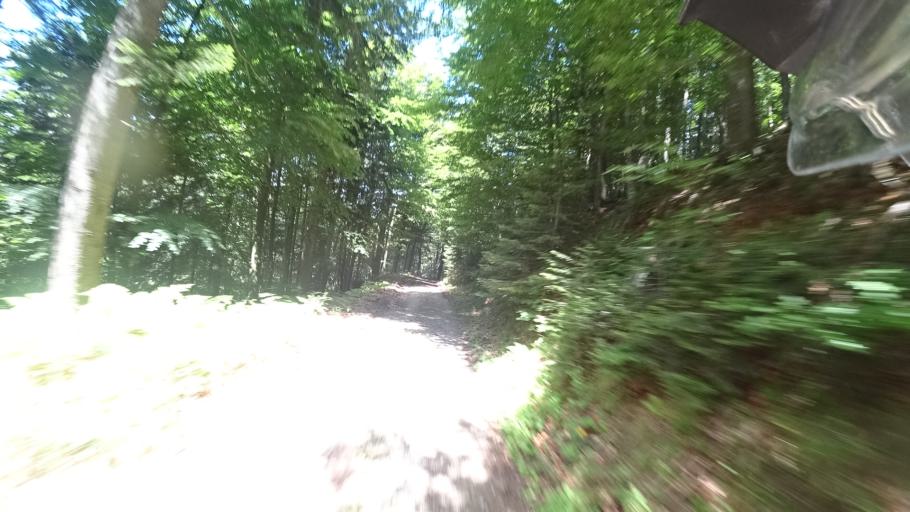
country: SI
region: Osilnica
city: Osilnica
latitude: 45.4690
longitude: 14.7275
